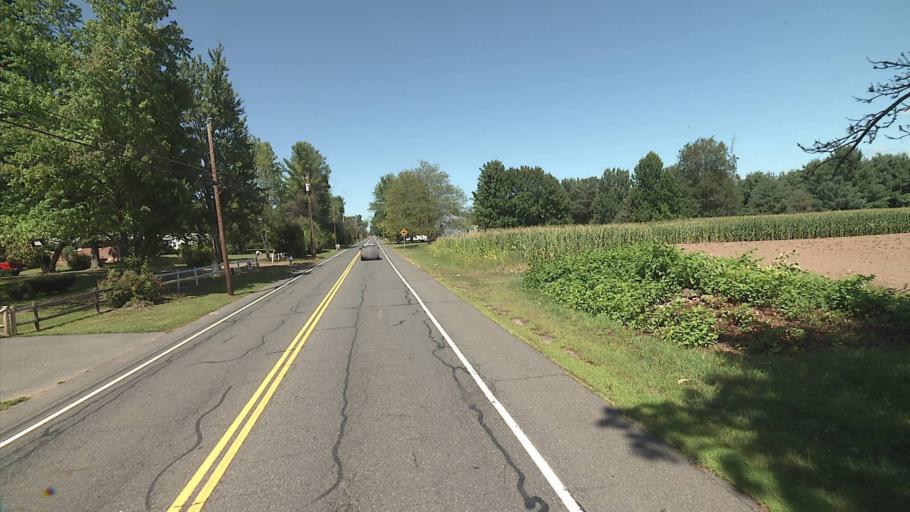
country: US
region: Connecticut
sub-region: Hartford County
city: Thompsonville
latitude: 42.0123
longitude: -72.6160
